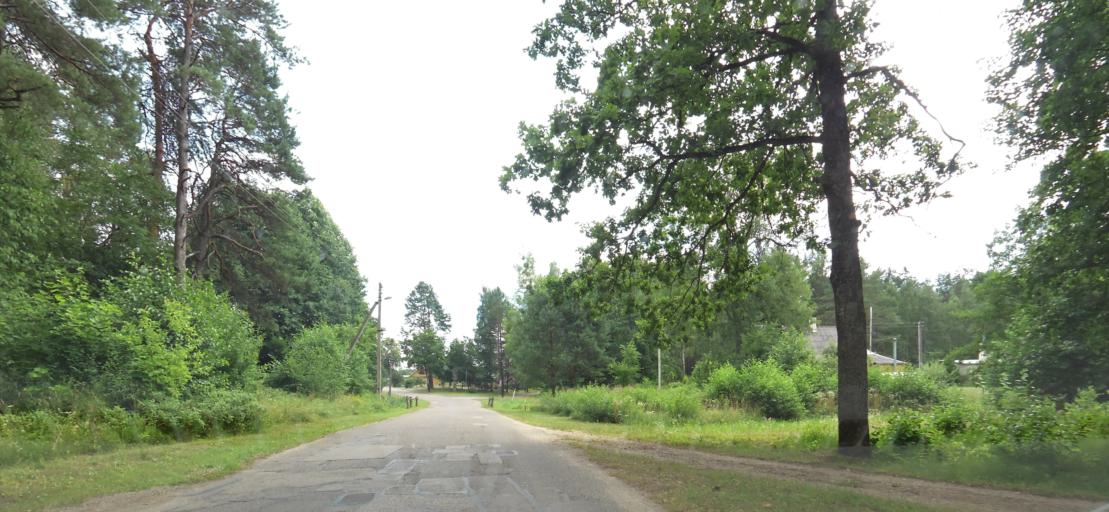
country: LT
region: Alytaus apskritis
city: Varena
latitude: 54.0590
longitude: 24.4008
